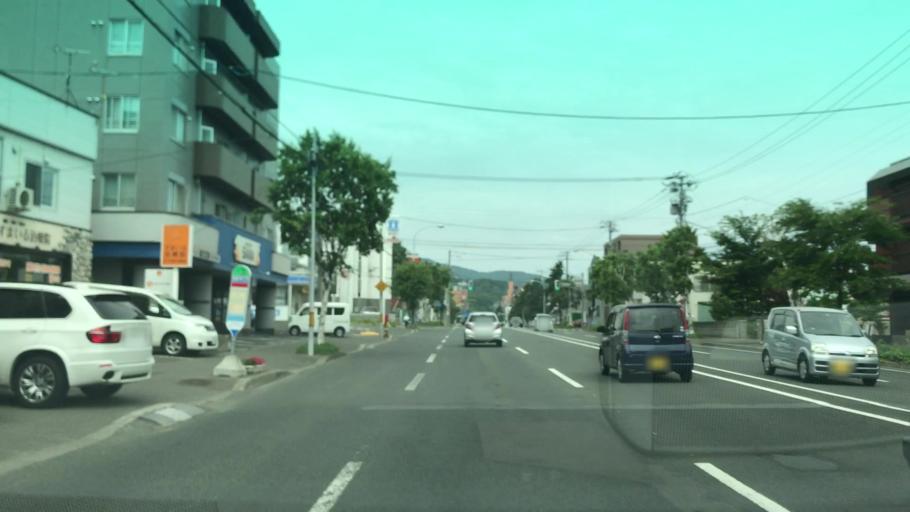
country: JP
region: Hokkaido
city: Sapporo
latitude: 43.0563
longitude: 141.3049
